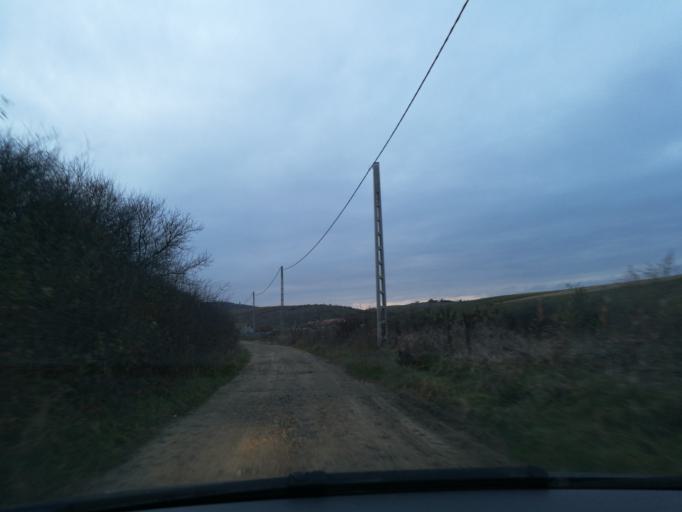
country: HU
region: Nograd
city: Bujak
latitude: 47.8653
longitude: 19.5634
